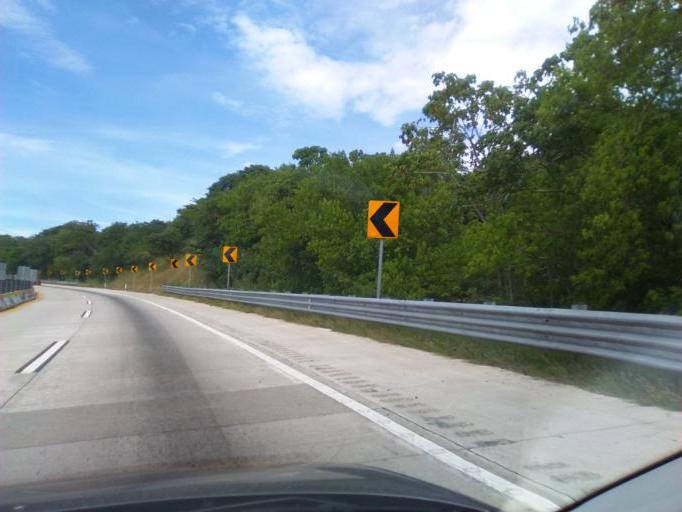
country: MX
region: Guerrero
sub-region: Chilpancingo de los Bravo
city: Julian Blanco (Dos Caminos)
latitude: 17.1997
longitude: -99.5327
